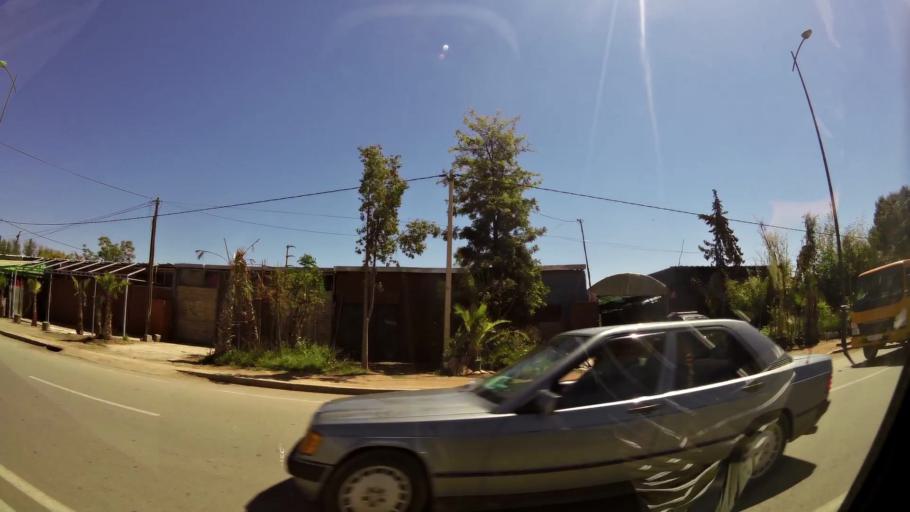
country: MA
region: Marrakech-Tensift-Al Haouz
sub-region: Marrakech
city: Marrakesh
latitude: 31.5718
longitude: -7.9807
